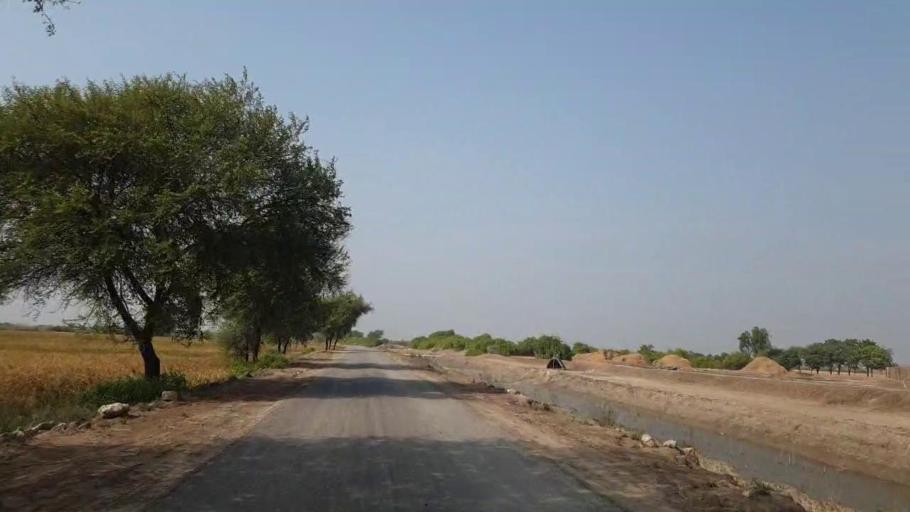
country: PK
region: Sindh
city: Matli
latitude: 24.9545
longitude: 68.5267
